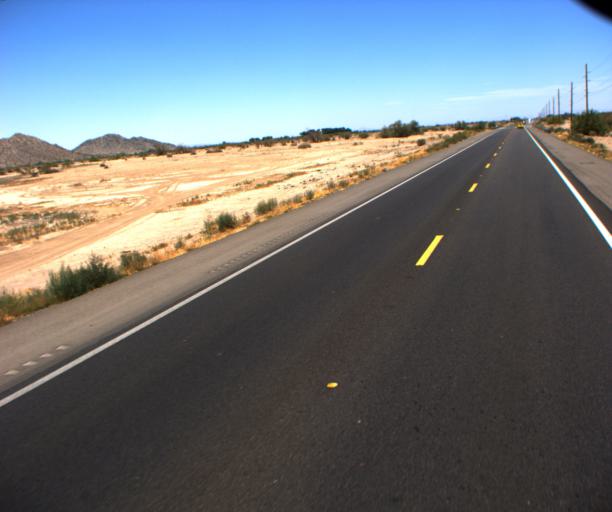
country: US
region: Arizona
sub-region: Pinal County
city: Casa Blanca
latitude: 33.1385
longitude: -111.8409
